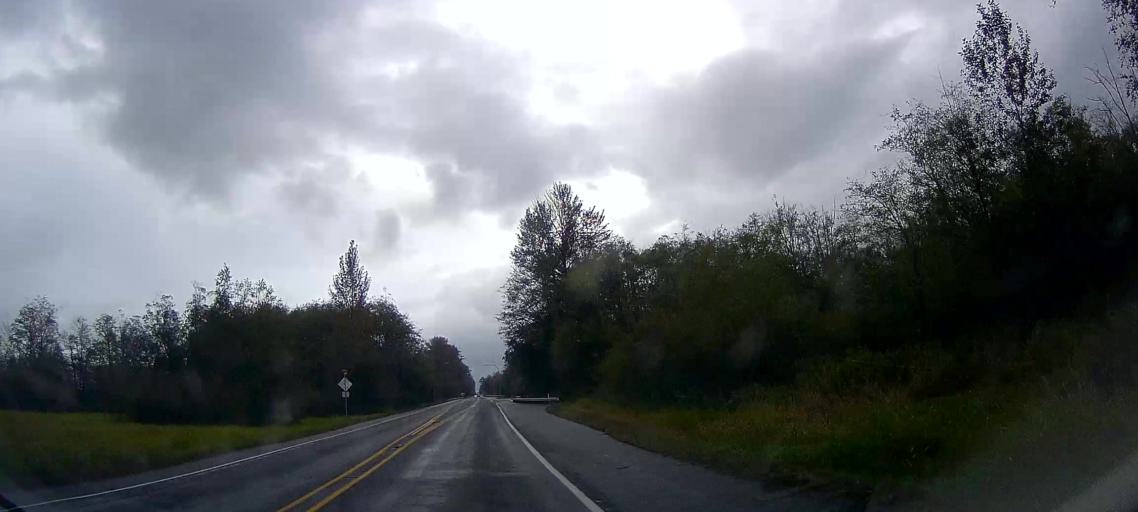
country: US
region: Washington
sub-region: Skagit County
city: Sedro-Woolley
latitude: 48.5245
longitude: -122.1924
